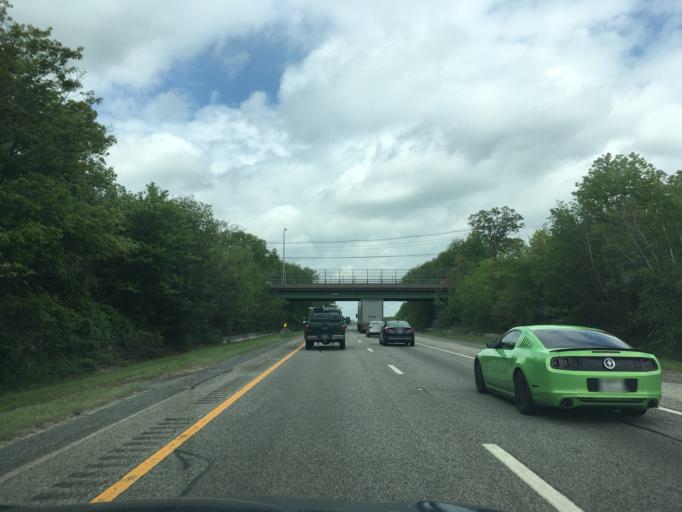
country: US
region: Rhode Island
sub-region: Providence County
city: Johnston
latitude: 41.8034
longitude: -71.5101
